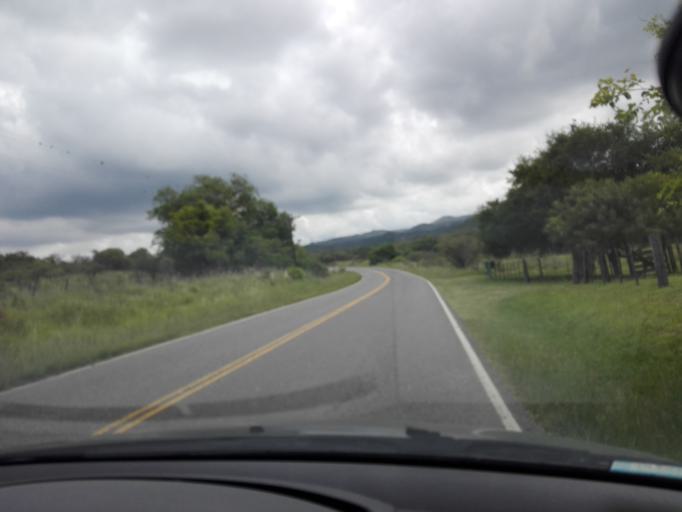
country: AR
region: Cordoba
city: Alta Gracia
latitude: -31.5862
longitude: -64.4794
